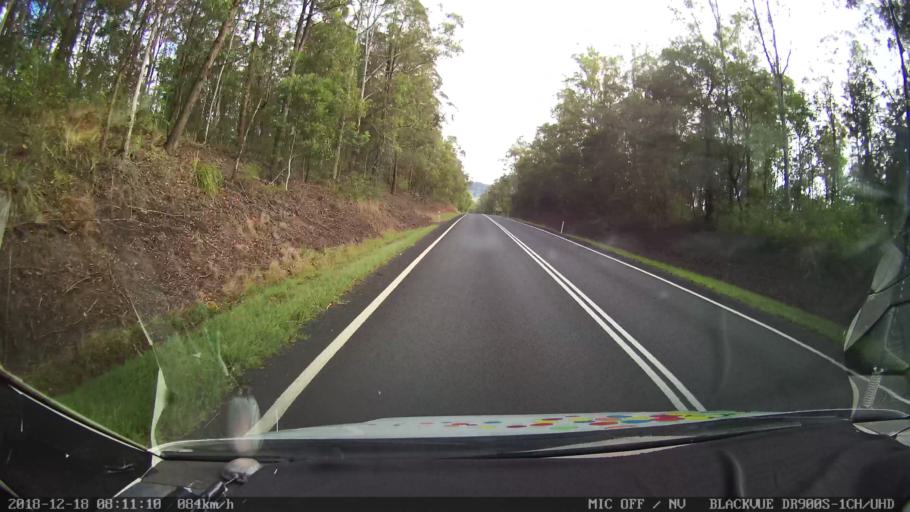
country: AU
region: New South Wales
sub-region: Kyogle
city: Kyogle
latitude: -28.3540
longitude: 152.6676
